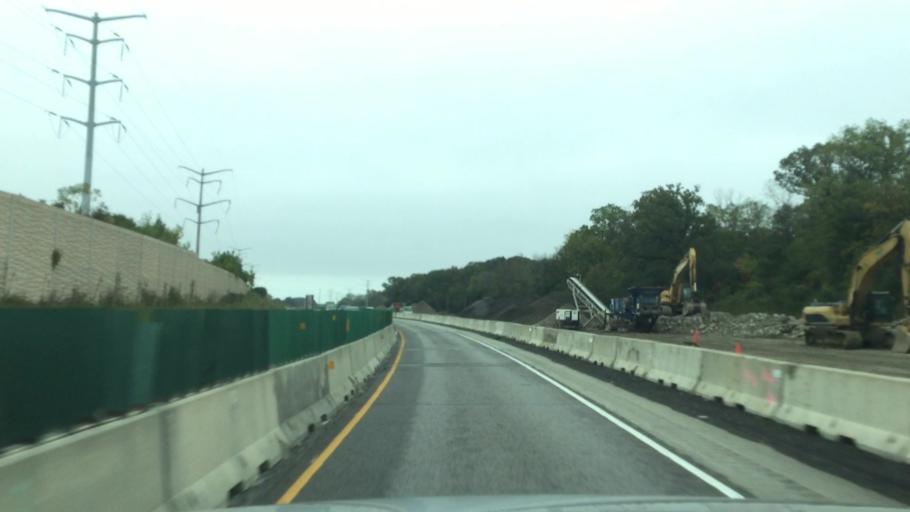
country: US
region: Illinois
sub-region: Cook County
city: Northbrook
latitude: 42.1444
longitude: -87.8274
